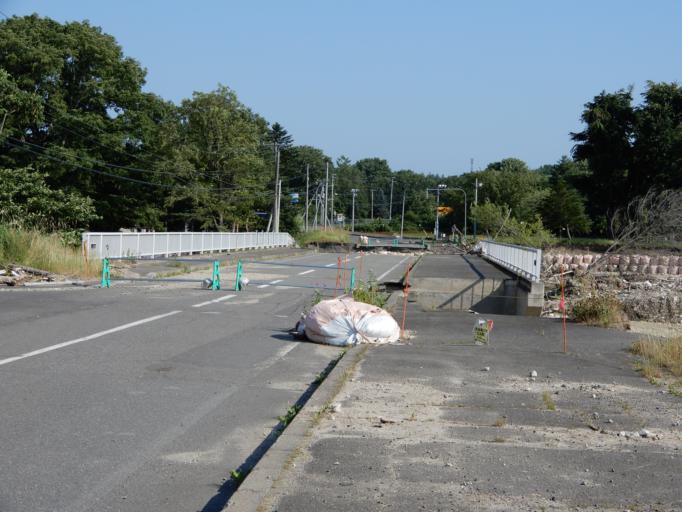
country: JP
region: Hokkaido
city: Otofuke
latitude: 43.0073
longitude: 142.8736
